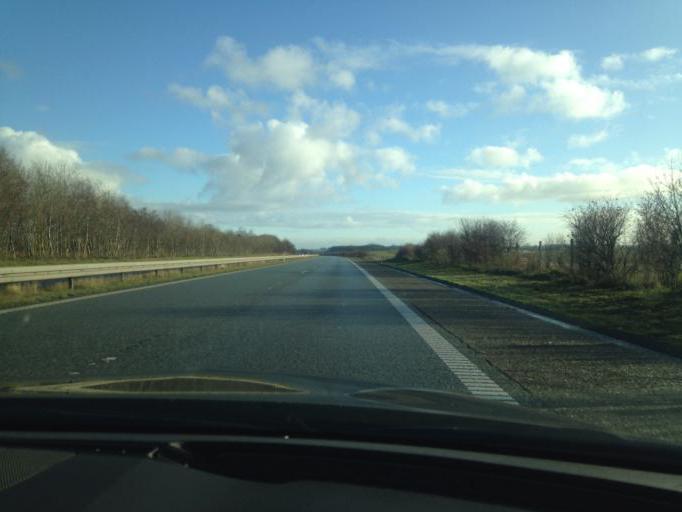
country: DK
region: South Denmark
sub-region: Vejen Kommune
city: Holsted
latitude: 55.5130
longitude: 8.9542
